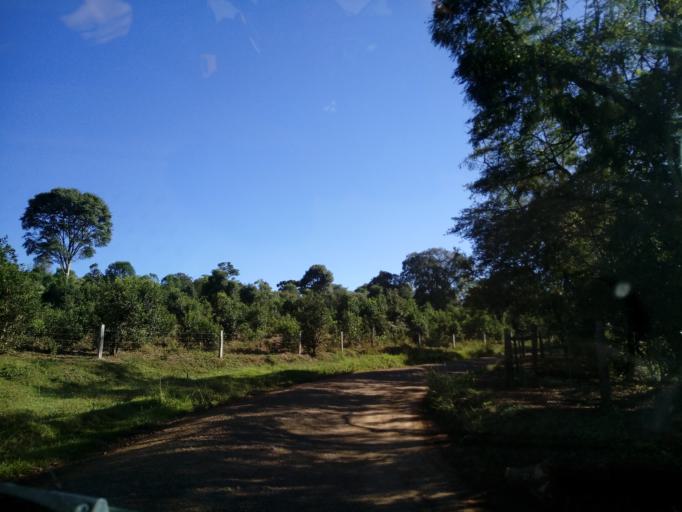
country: BR
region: Santa Catarina
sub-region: Chapeco
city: Chapeco
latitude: -27.1943
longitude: -52.7081
